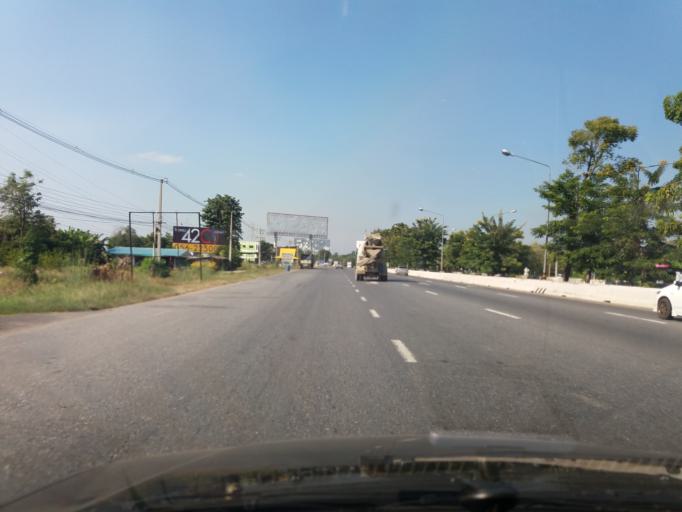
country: TH
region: Nakhon Sawan
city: Krok Phra
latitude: 15.6112
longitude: 100.1212
